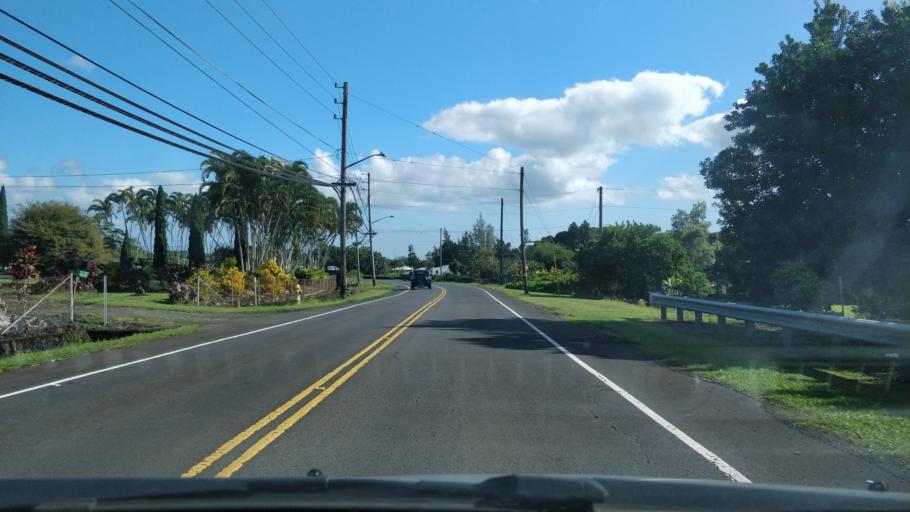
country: US
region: Hawaii
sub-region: Hawaii County
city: Hilo
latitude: 19.6660
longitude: -155.0976
